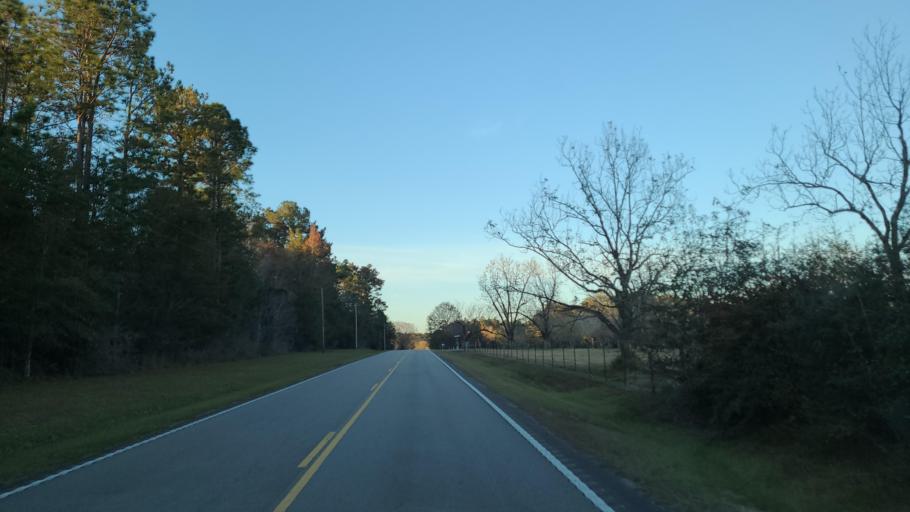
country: US
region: Mississippi
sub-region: Stone County
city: Wiggins
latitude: 31.0071
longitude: -89.2571
